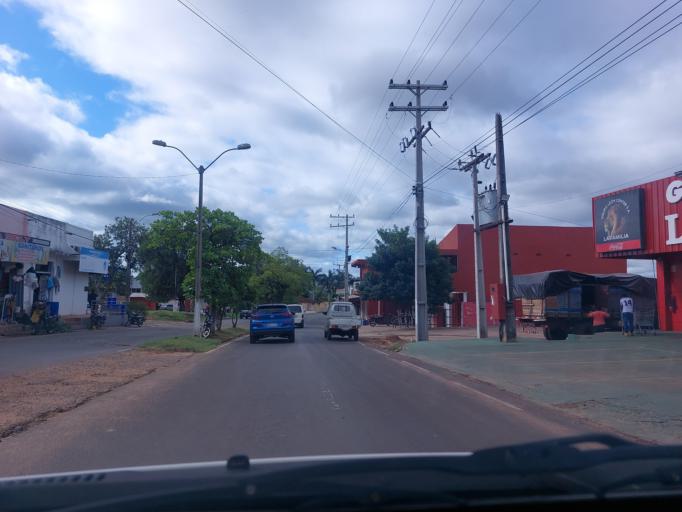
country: PY
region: San Pedro
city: Guayaybi
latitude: -24.6666
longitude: -56.4395
